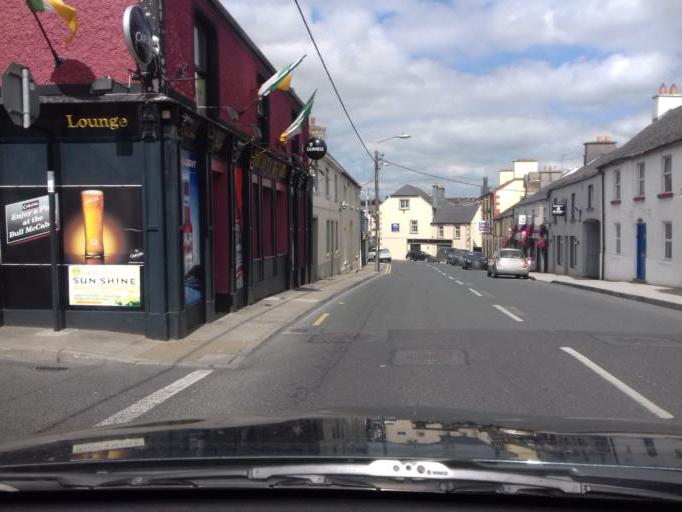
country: IE
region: Leinster
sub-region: County Carlow
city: Tullow
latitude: 52.8012
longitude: -6.7391
